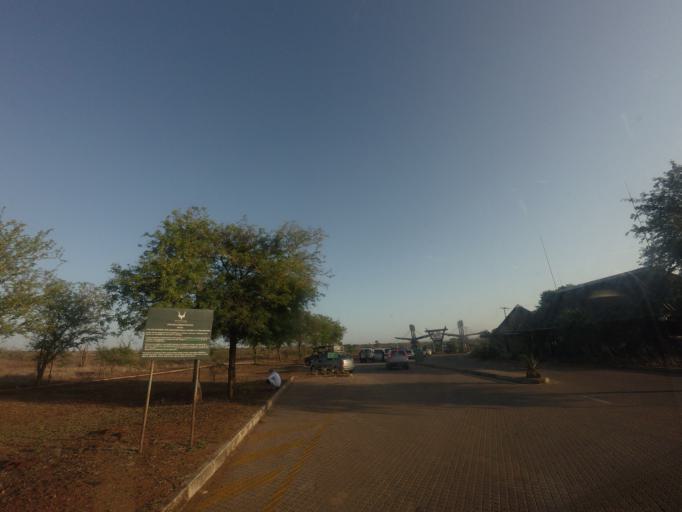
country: ZA
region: Mpumalanga
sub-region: Ehlanzeni District
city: Komatipoort
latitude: -25.3592
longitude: 31.8923
